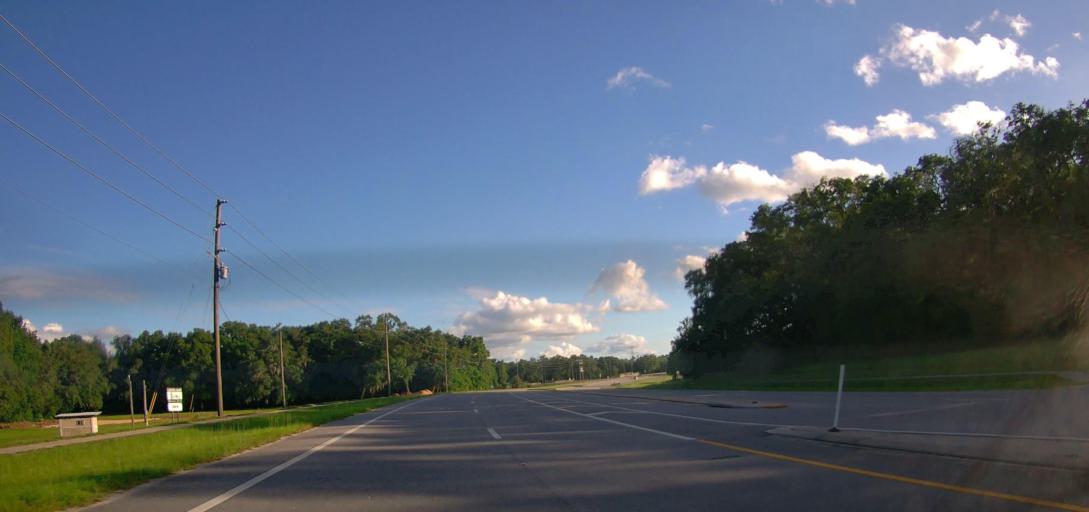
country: US
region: Florida
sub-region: Marion County
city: Belleview
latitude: 29.0349
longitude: -82.0178
